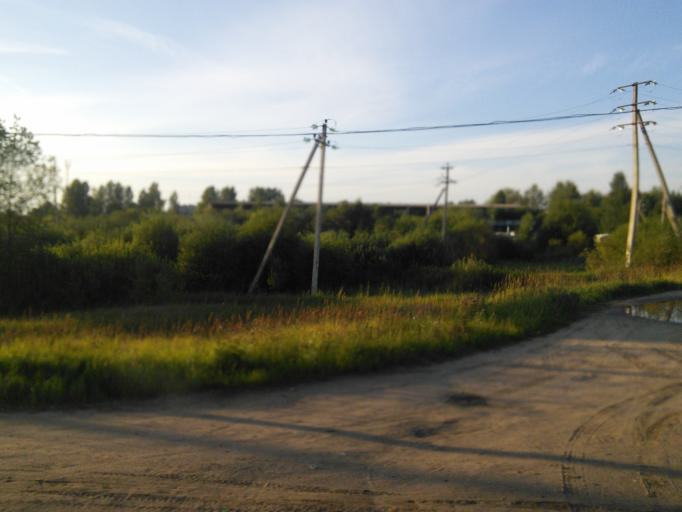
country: RU
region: Vologda
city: Chagoda
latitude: 59.1604
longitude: 35.3285
